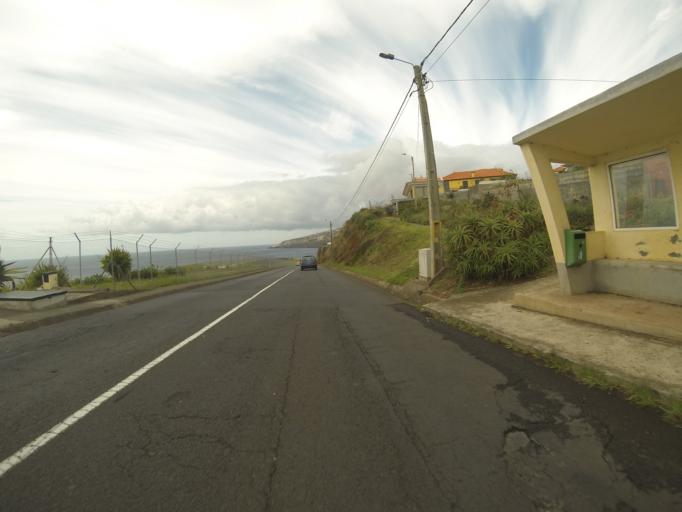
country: PT
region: Madeira
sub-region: Machico
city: Machico
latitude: 32.6930
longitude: -16.7823
